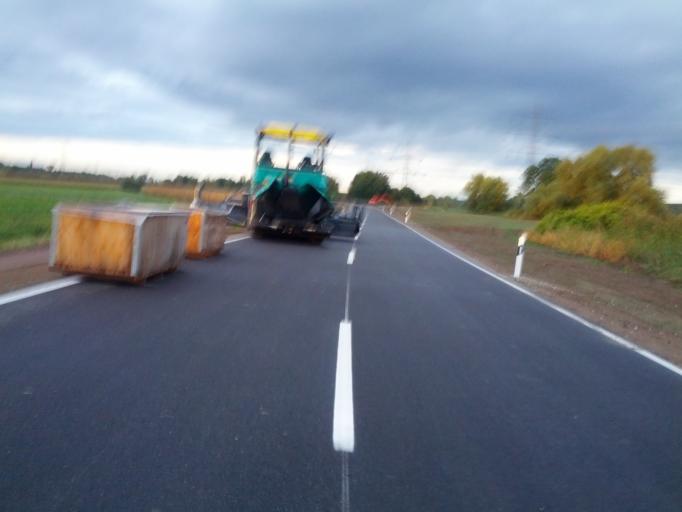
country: DE
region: Baden-Wuerttemberg
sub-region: Freiburg Region
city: Eichstetten
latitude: 48.0768
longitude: 7.7520
